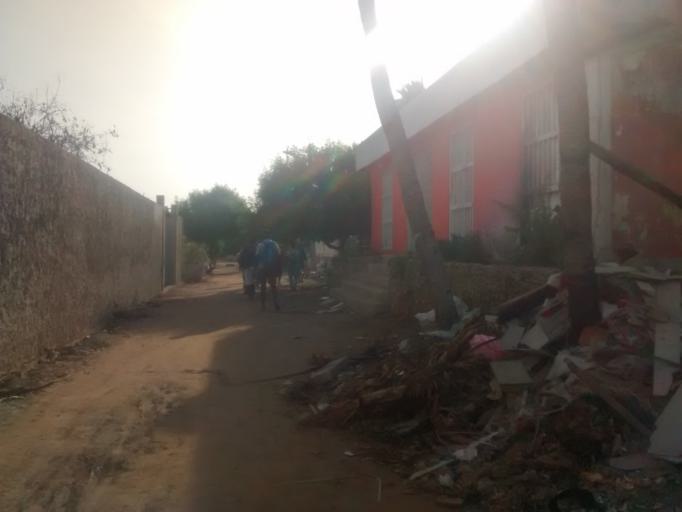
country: CO
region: Bolivar
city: Turbana
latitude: 10.1403
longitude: -75.6850
